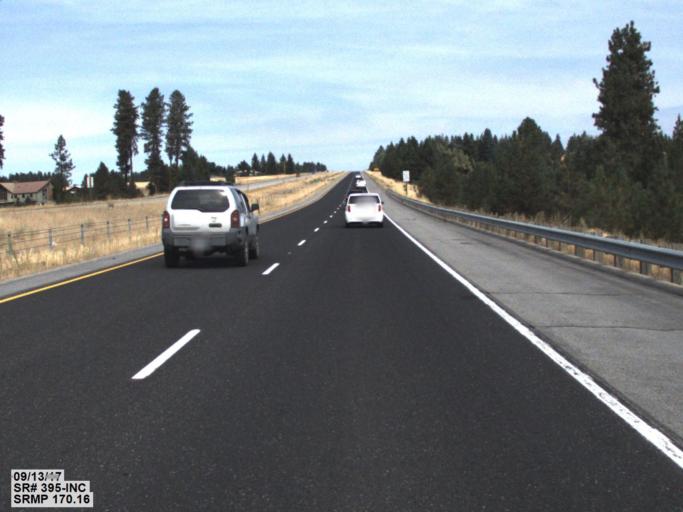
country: US
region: Washington
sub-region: Spokane County
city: Fairwood
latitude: 47.8190
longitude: -117.4115
